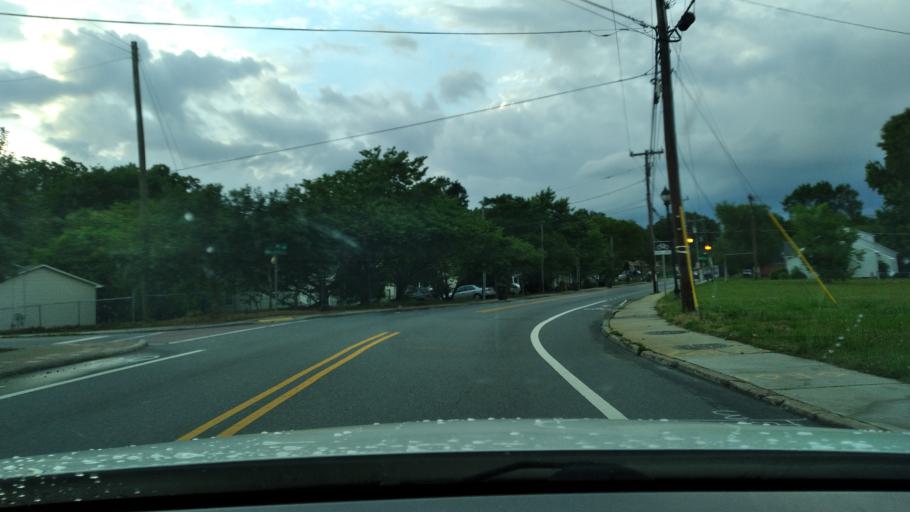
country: US
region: North Carolina
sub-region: Guilford County
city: Greensboro
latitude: 36.0563
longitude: -79.7846
